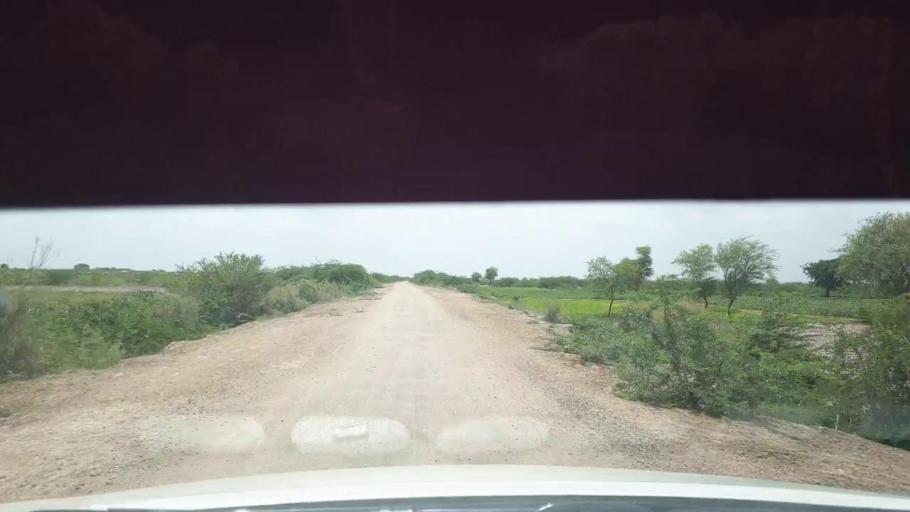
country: PK
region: Sindh
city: Kadhan
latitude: 24.5261
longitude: 69.0942
